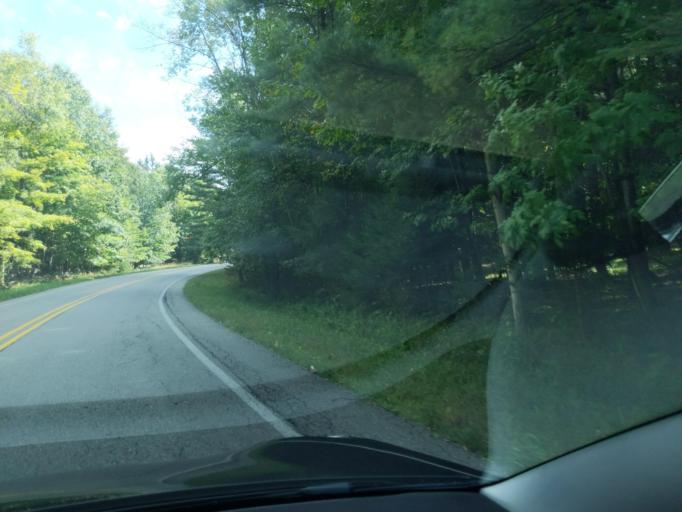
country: US
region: Michigan
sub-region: Antrim County
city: Bellaire
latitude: 45.0475
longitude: -85.3064
